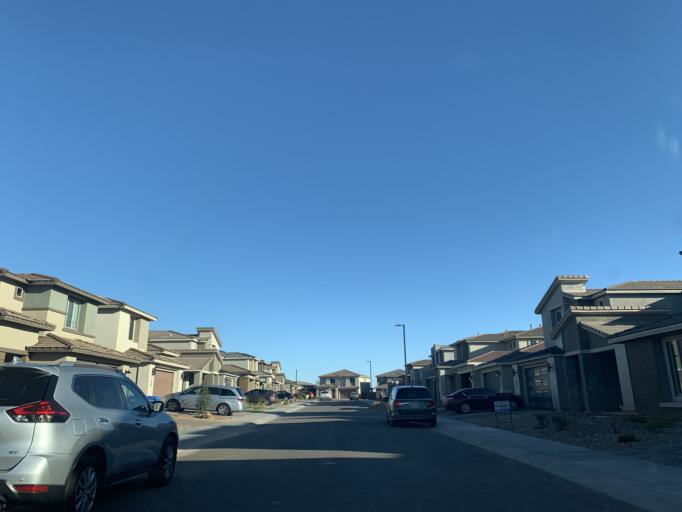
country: US
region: Arizona
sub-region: Maricopa County
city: Cave Creek
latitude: 33.6858
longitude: -112.0187
